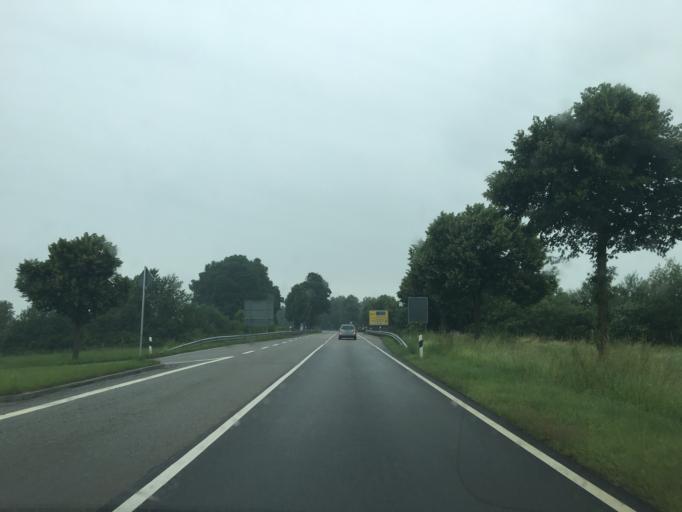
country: DE
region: Bavaria
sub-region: Upper Bavaria
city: Holzkirchen
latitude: 47.8579
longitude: 11.7176
